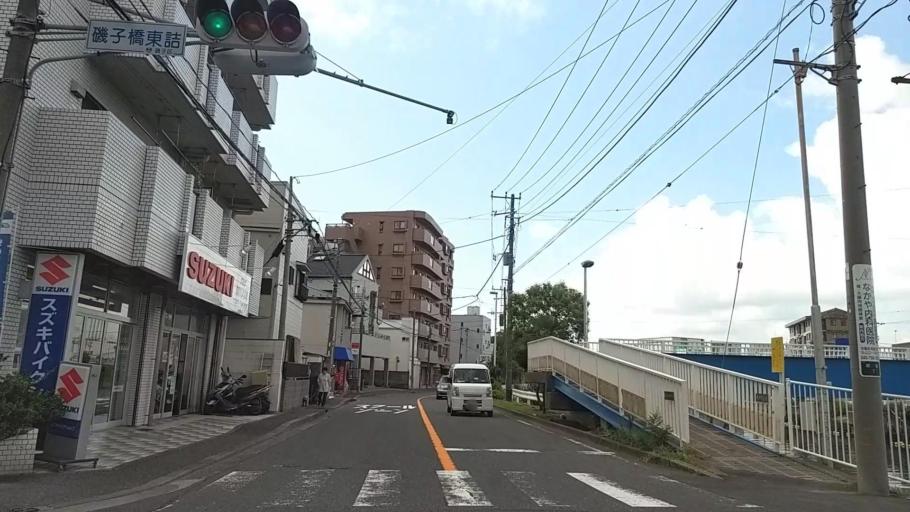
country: JP
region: Kanagawa
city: Yokohama
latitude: 35.4173
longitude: 139.6271
